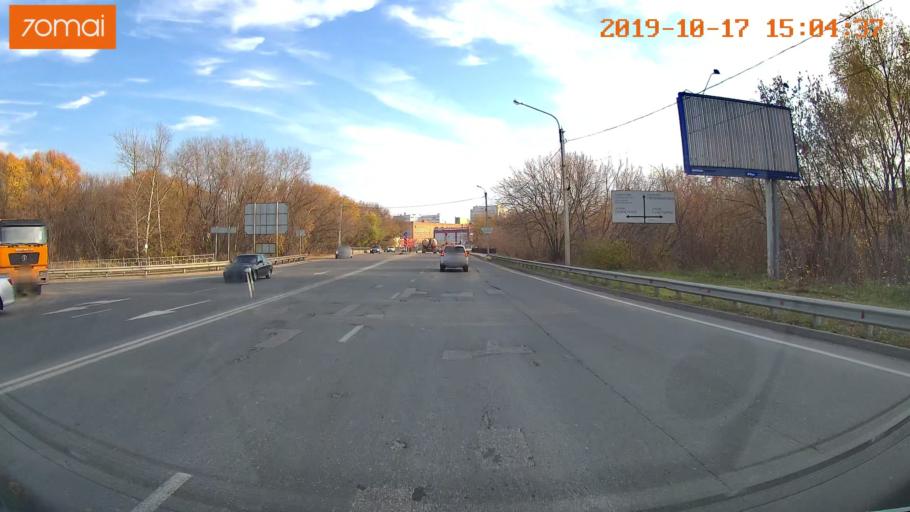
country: RU
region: Rjazan
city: Ryazan'
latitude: 54.6386
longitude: 39.7209
